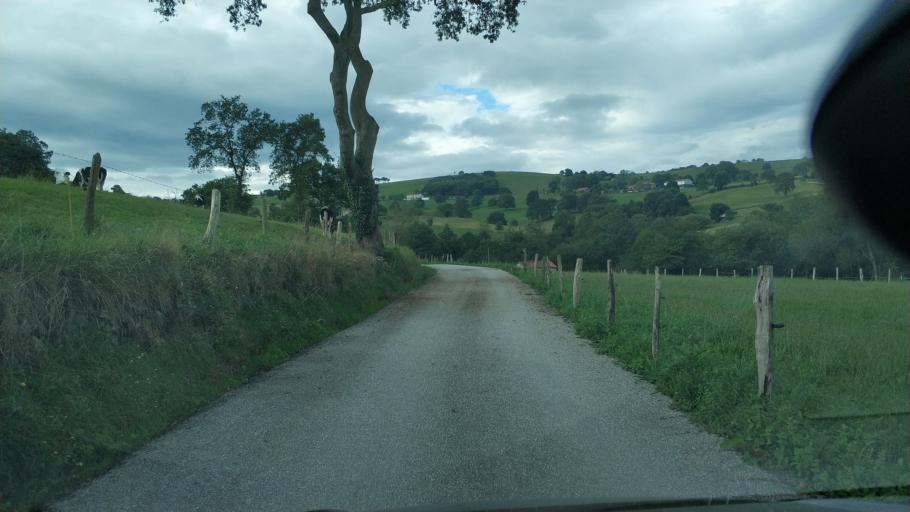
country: ES
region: Cantabria
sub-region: Provincia de Cantabria
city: Santa Maria de Cayon
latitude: 43.2810
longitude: -3.8105
